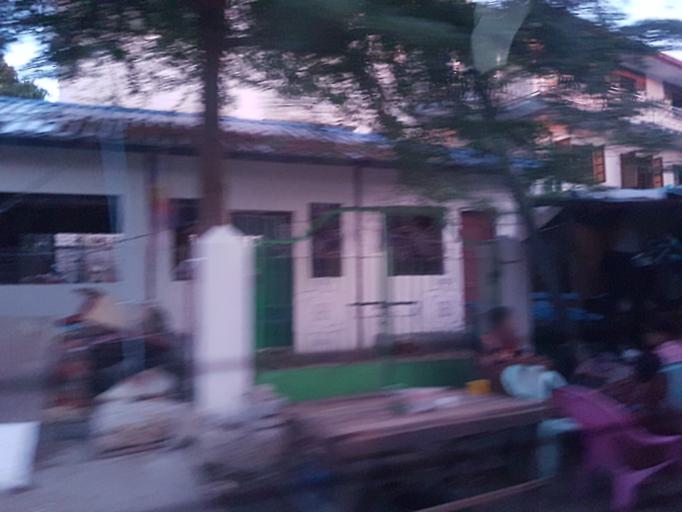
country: MM
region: Yangon
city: Yangon
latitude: 16.8043
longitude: 96.1641
